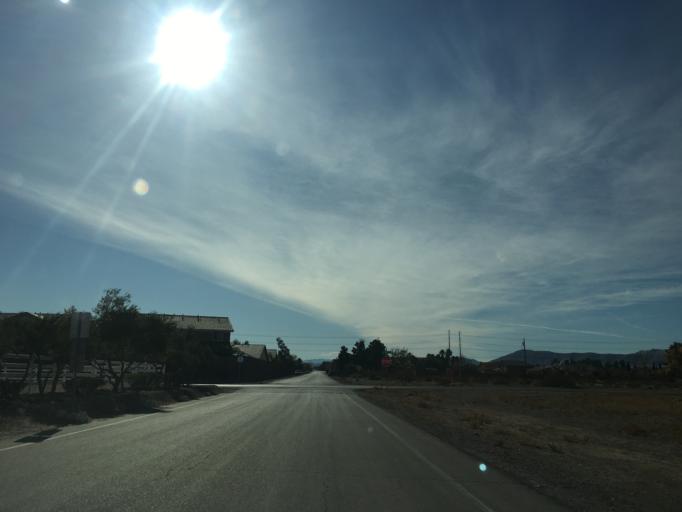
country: US
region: Nevada
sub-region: Clark County
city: Enterprise
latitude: 36.0072
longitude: -115.1658
